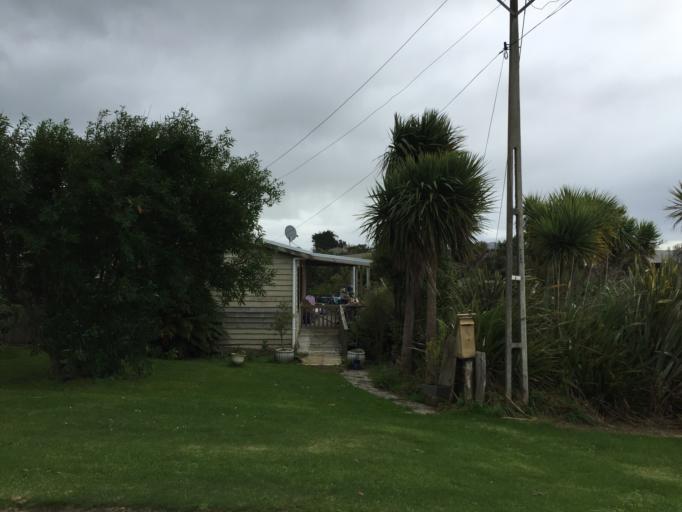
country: NZ
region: Southland
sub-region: Southland District
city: Riverton
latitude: -46.3729
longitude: 168.0263
